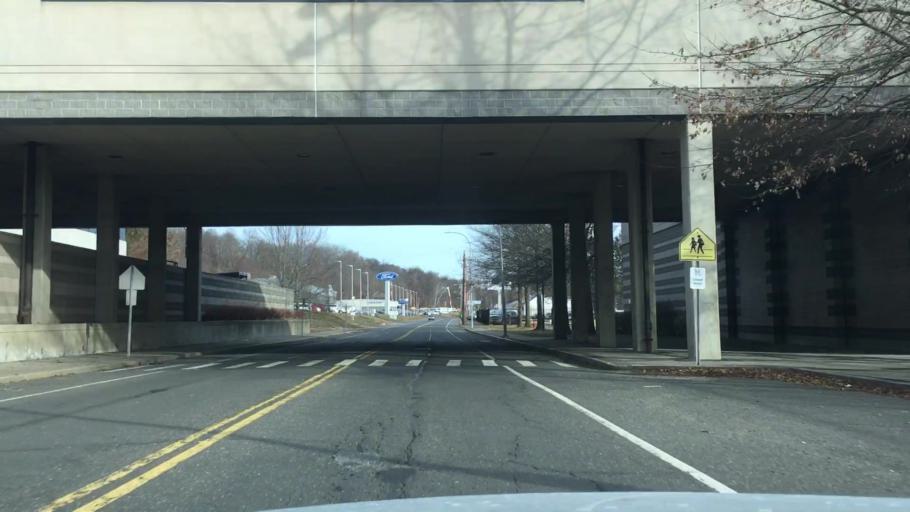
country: US
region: Massachusetts
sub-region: Hampden County
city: Holyoke
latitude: 42.1784
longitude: -72.6297
